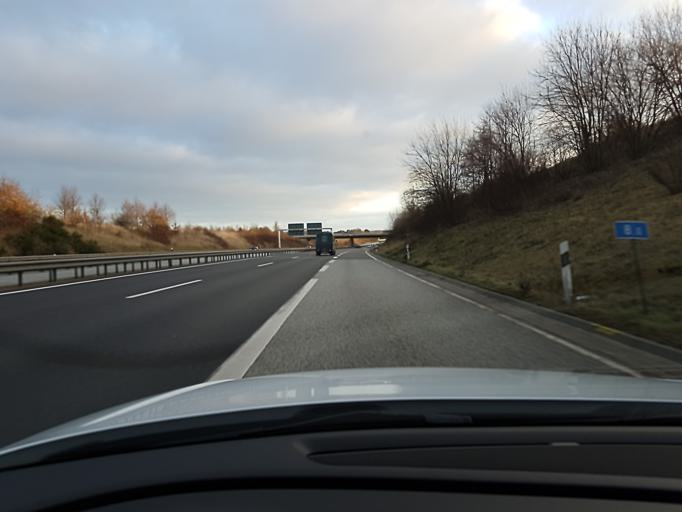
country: DE
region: Schleswig-Holstein
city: Hamberge
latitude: 53.8458
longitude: 10.6032
